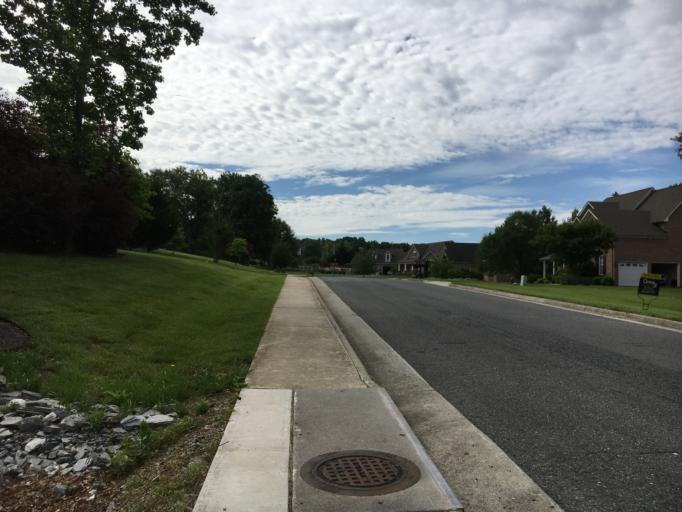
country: US
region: Virginia
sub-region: Bedford County
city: Forest
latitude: 37.3690
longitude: -79.2646
